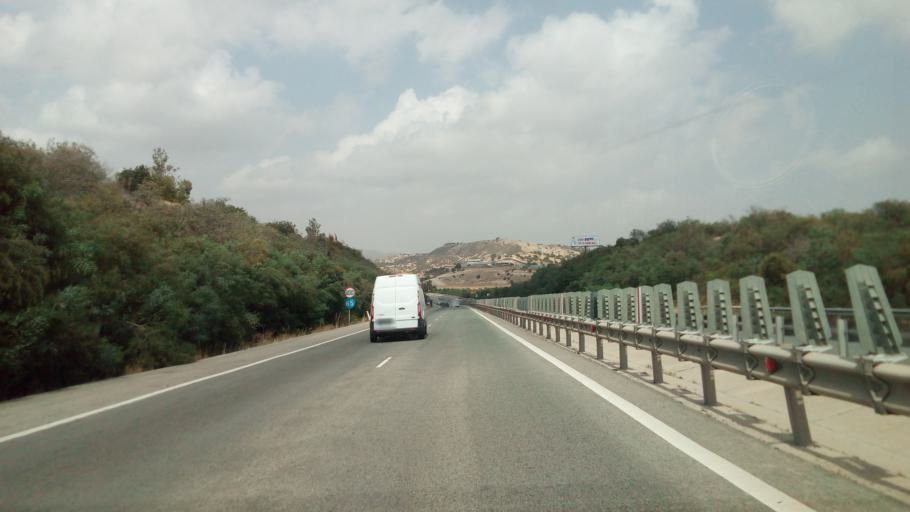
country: CY
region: Larnaka
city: Kofinou
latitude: 34.8201
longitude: 33.3692
